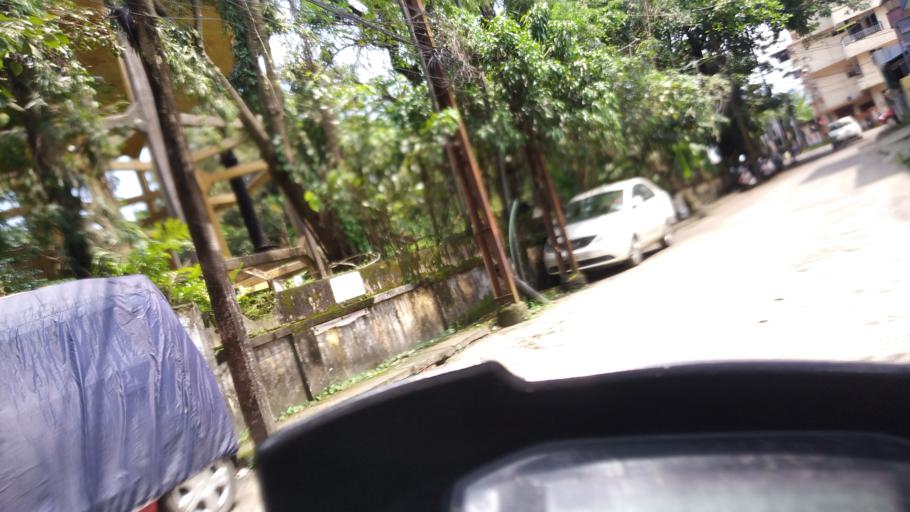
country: IN
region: Kerala
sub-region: Ernakulam
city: Cochin
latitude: 9.9586
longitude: 76.2920
